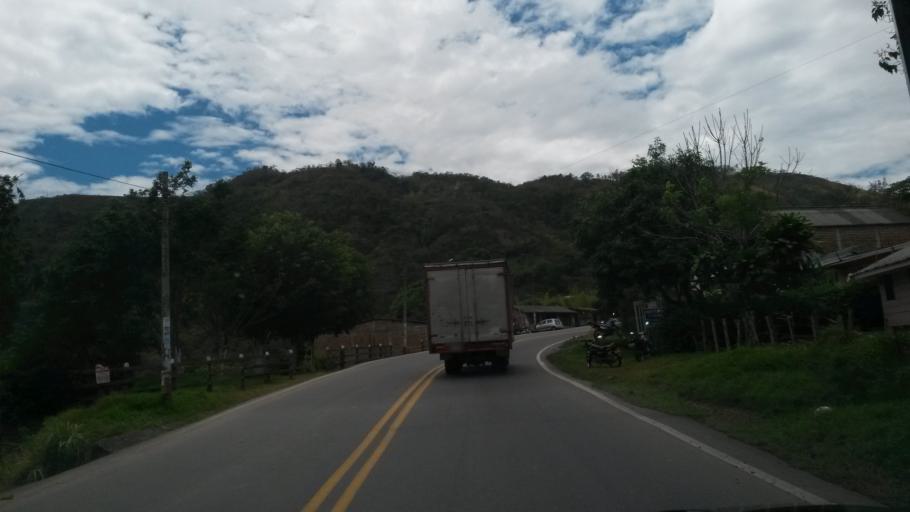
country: CO
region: Cauca
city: Rosas
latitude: 2.2638
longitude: -76.7390
